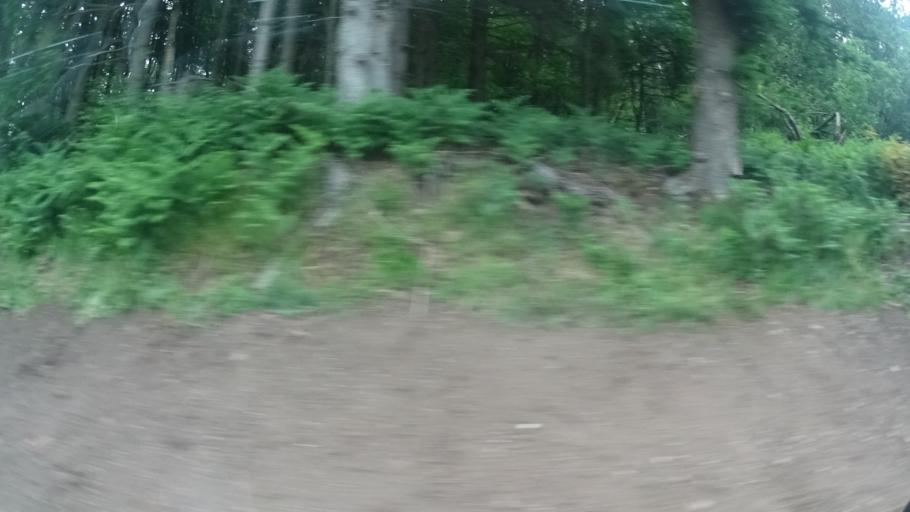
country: DE
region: Bavaria
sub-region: Regierungsbezirk Unterfranken
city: Kleinkahl
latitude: 50.1229
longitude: 9.3108
